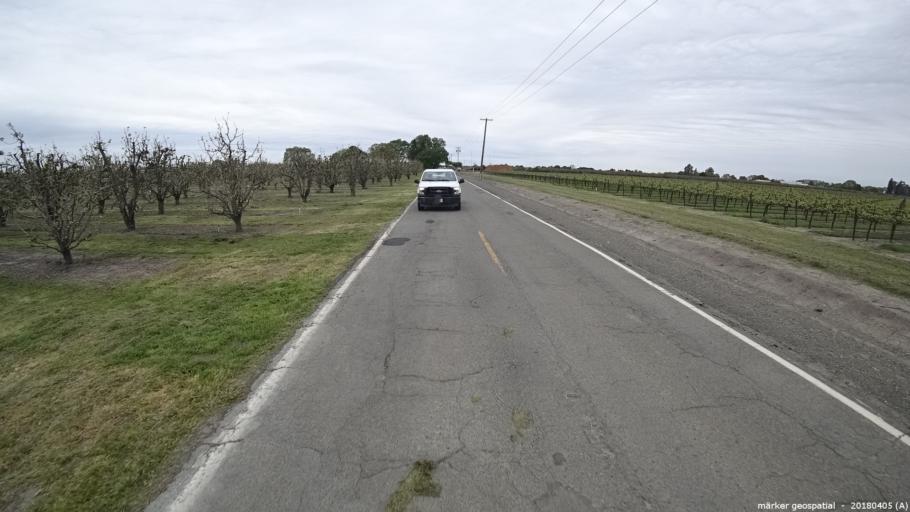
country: US
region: California
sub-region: Sacramento County
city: Walnut Grove
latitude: 38.3380
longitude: -121.5386
